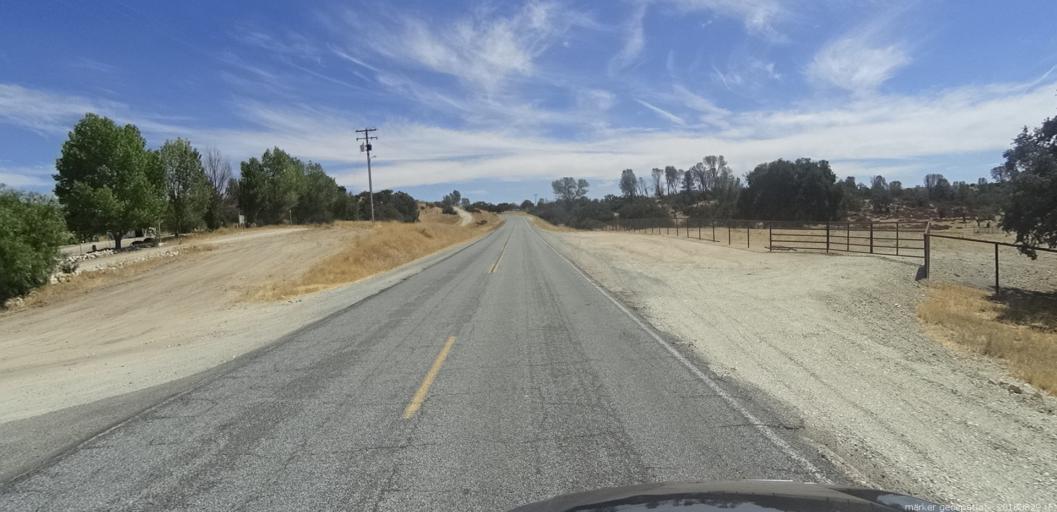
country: US
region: California
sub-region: San Luis Obispo County
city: Lake Nacimiento
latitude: 35.9069
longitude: -120.9988
